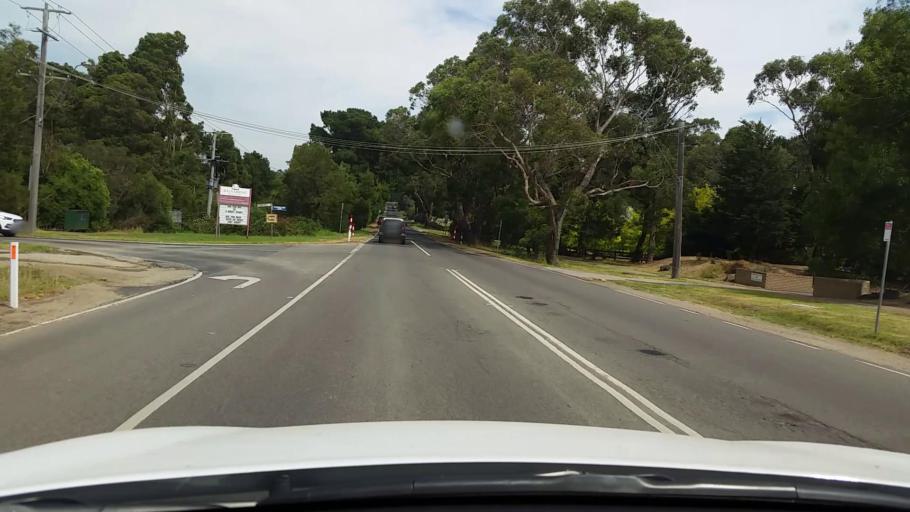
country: AU
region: Victoria
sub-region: Mornington Peninsula
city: Balnarring
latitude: -38.3739
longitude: 145.1227
